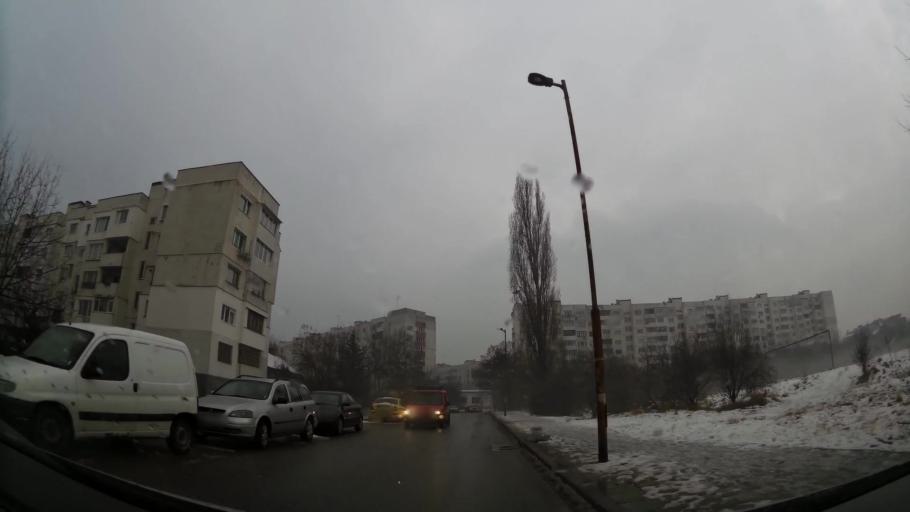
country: BG
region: Sofia-Capital
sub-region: Stolichna Obshtina
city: Sofia
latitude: 42.6853
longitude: 23.2638
